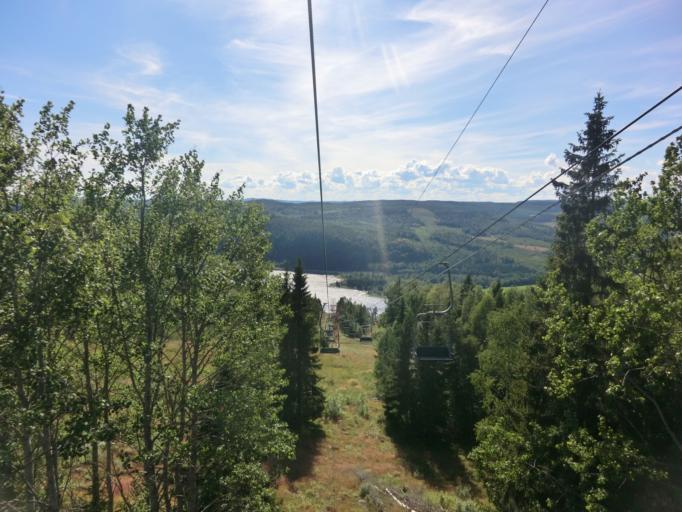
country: SE
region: Vaesternorrland
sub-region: Kramfors Kommun
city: Nordingra
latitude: 63.0746
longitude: 18.3445
